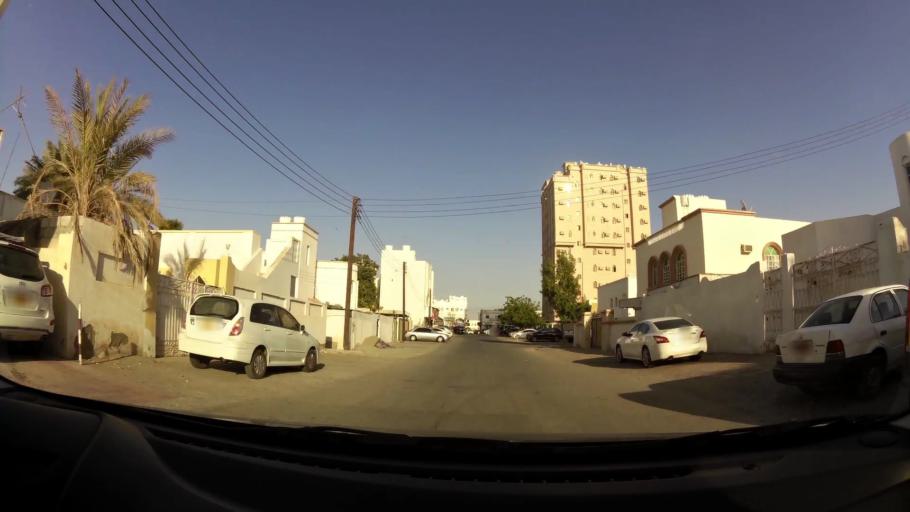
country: OM
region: Muhafazat Masqat
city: As Sib al Jadidah
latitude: 23.6295
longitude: 58.1954
